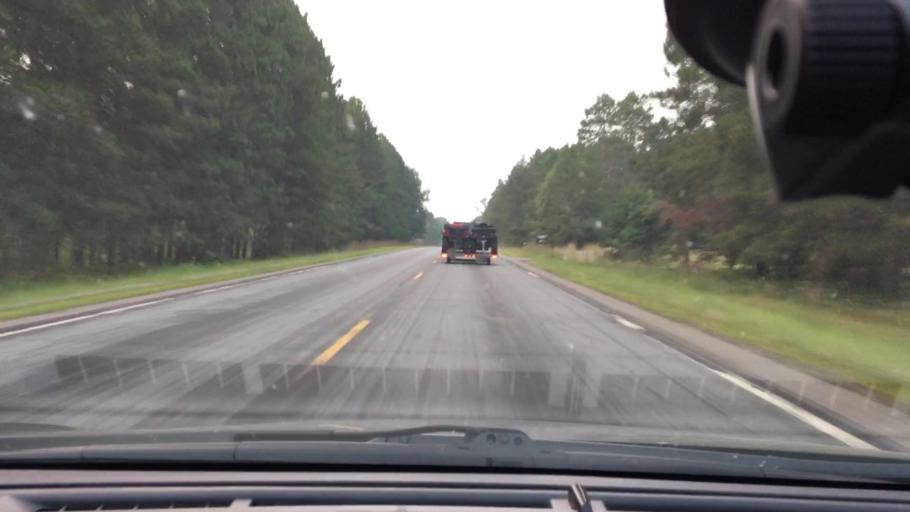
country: US
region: Minnesota
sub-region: Crow Wing County
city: Cross Lake
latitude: 46.7669
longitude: -93.9664
